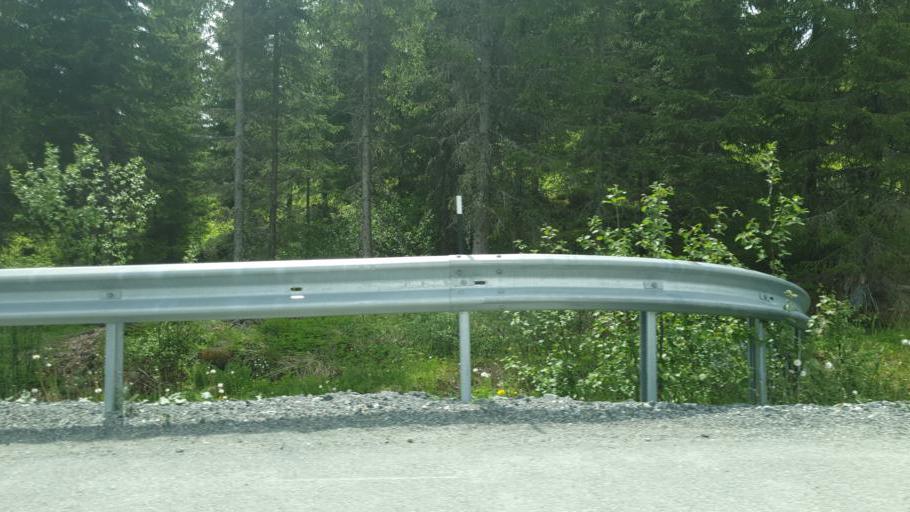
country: NO
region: Nord-Trondelag
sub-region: Leksvik
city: Leksvik
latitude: 63.6866
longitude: 10.5378
